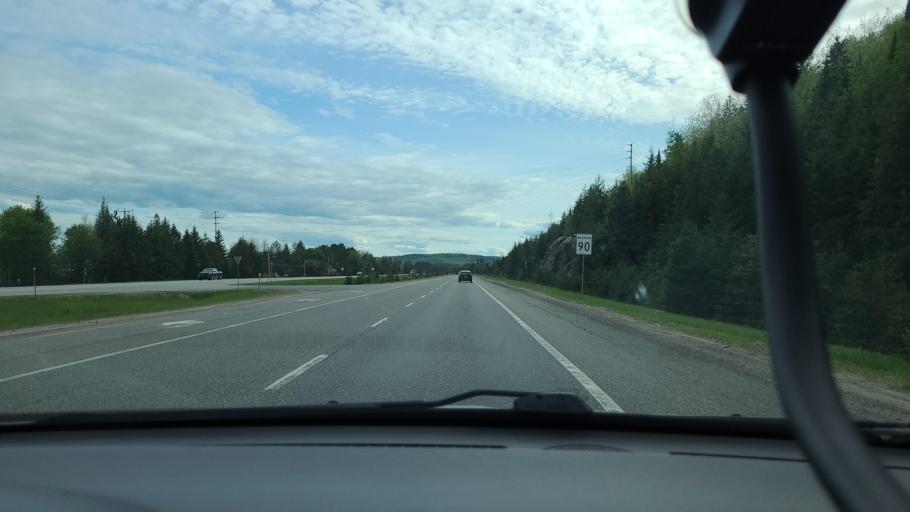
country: CA
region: Quebec
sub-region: Laurentides
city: Labelle
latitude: 46.2143
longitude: -74.7119
